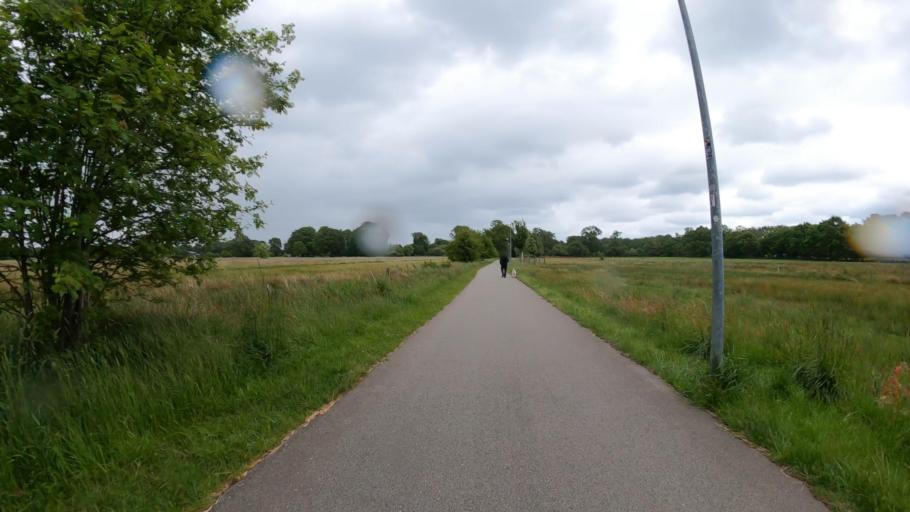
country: DE
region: Hamburg
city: Langenhorn
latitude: 53.6991
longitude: 10.0179
